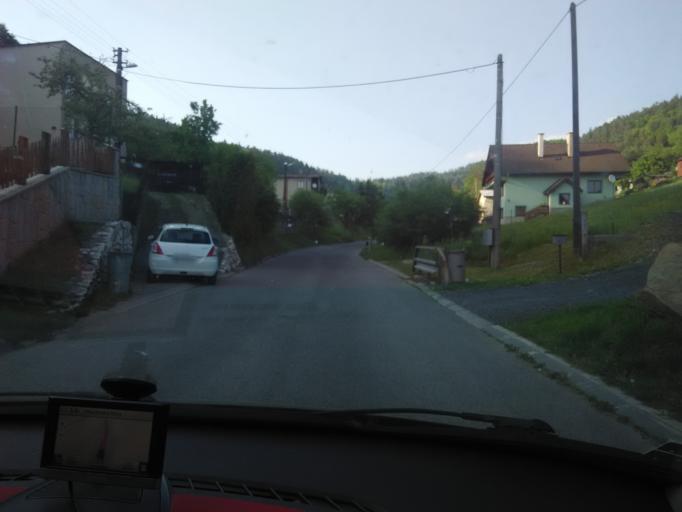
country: SK
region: Presovsky
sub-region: Okres Presov
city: Levoca
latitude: 49.0351
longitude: 20.6005
